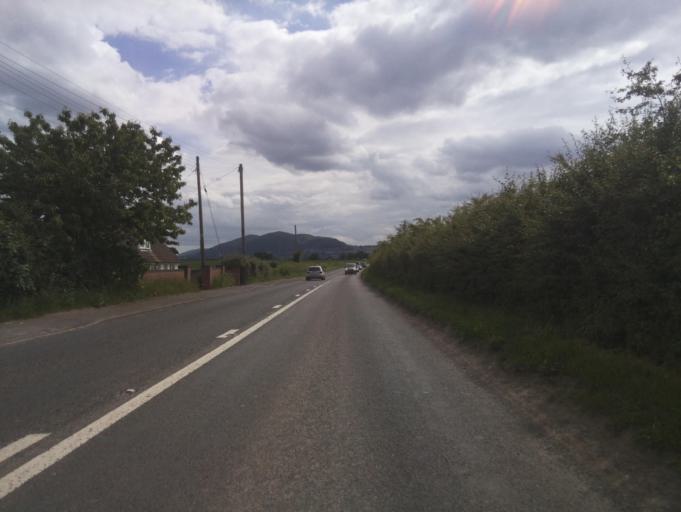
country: GB
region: England
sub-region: Worcestershire
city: Bransford
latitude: 52.1621
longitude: -2.3099
